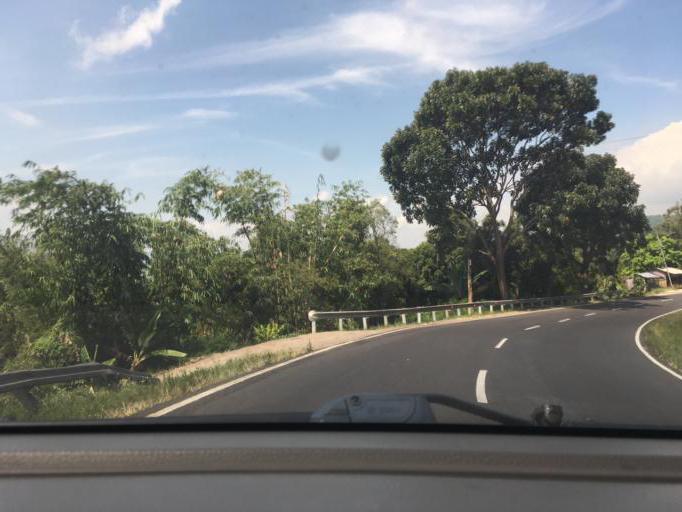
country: ID
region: West Java
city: Wage Cibahayu
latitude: -7.1146
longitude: 108.1166
